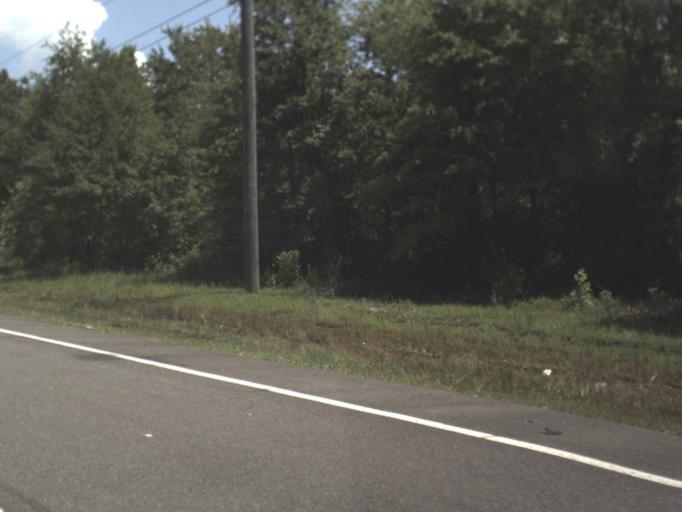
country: US
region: Florida
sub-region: Nassau County
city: Nassau Village-Ratliff
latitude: 30.4739
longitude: -81.7113
